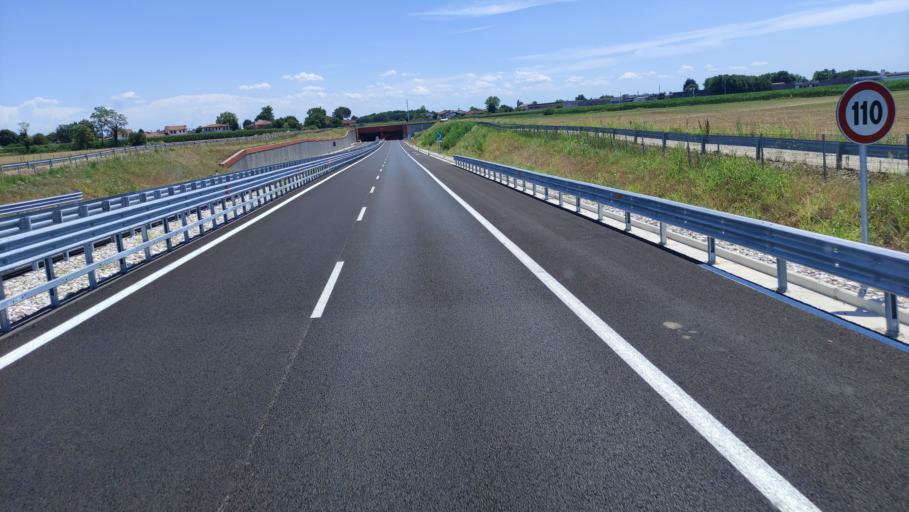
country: IT
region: Veneto
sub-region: Provincia di Treviso
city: San Vito
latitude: 45.7507
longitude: 11.9034
